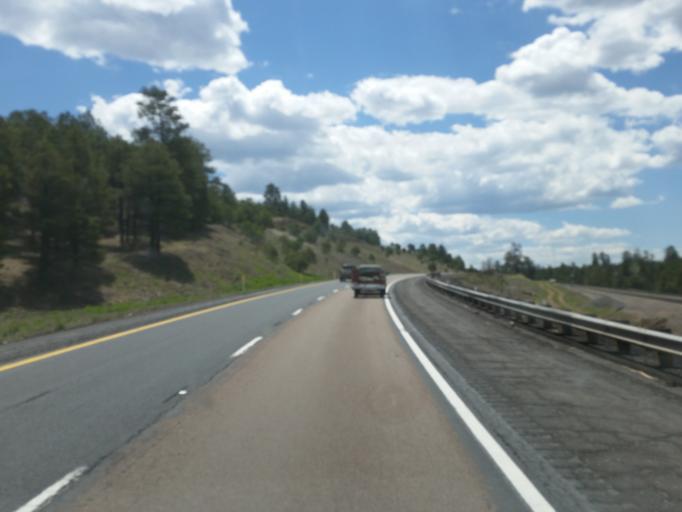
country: US
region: Arizona
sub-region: Coconino County
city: Flagstaff
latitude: 35.2110
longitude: -111.7737
